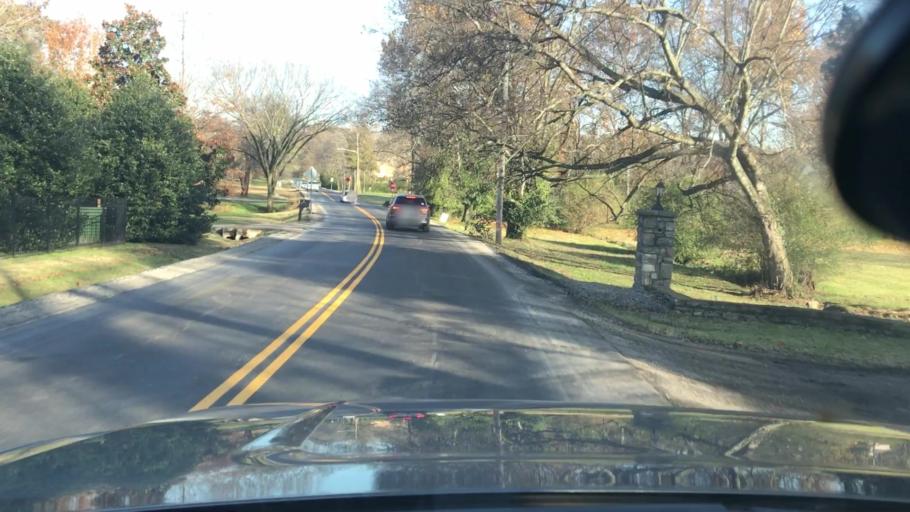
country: US
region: Tennessee
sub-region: Davidson County
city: Belle Meade
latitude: 36.1033
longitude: -86.8838
